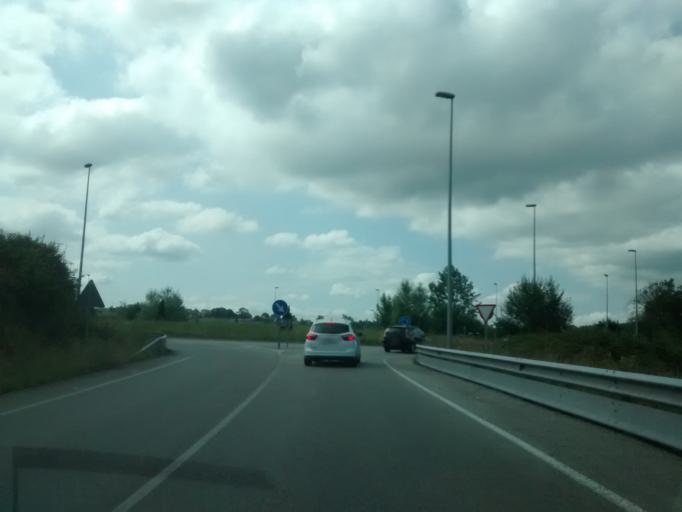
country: ES
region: Asturias
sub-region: Province of Asturias
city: Pola de Siero
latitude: 43.3866
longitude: -5.6658
